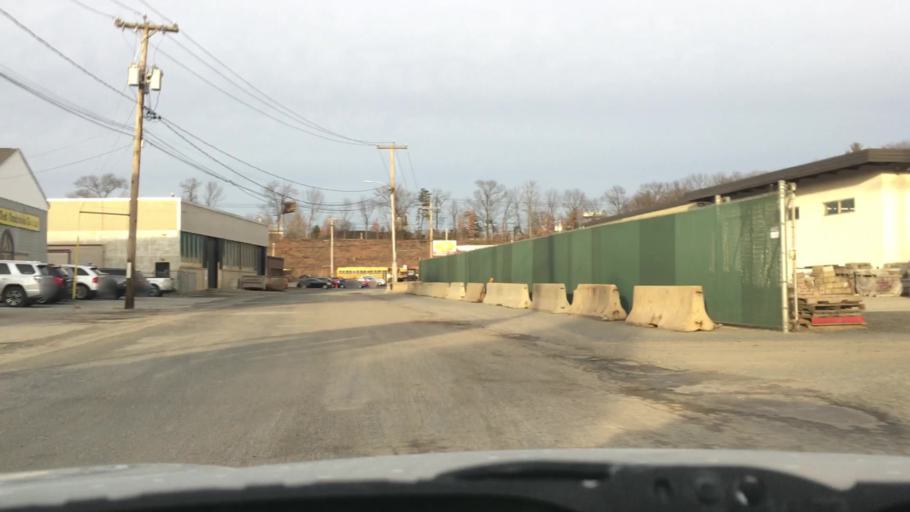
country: US
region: Massachusetts
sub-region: Hampden County
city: North Chicopee
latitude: 42.1586
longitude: -72.5528
